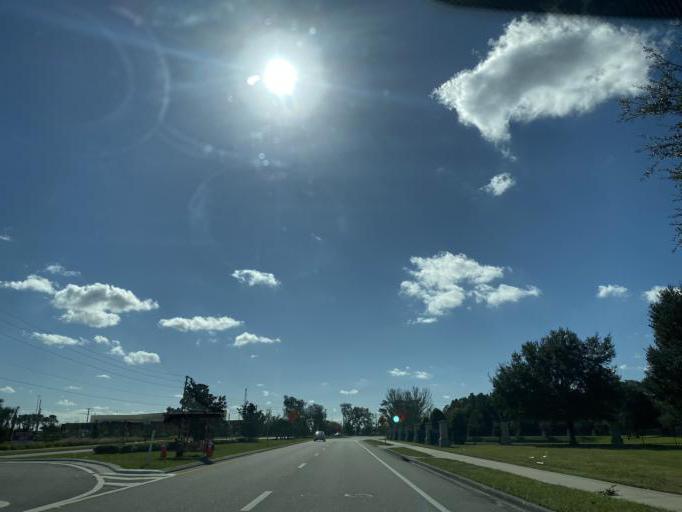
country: US
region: Florida
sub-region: Seminole County
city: Heathrow
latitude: 28.8030
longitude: -81.3481
